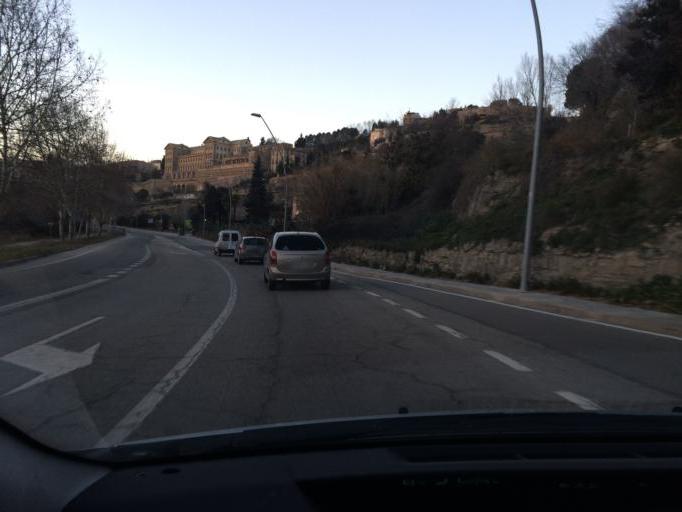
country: ES
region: Catalonia
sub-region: Provincia de Barcelona
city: Manresa
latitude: 41.7185
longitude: 1.8330
